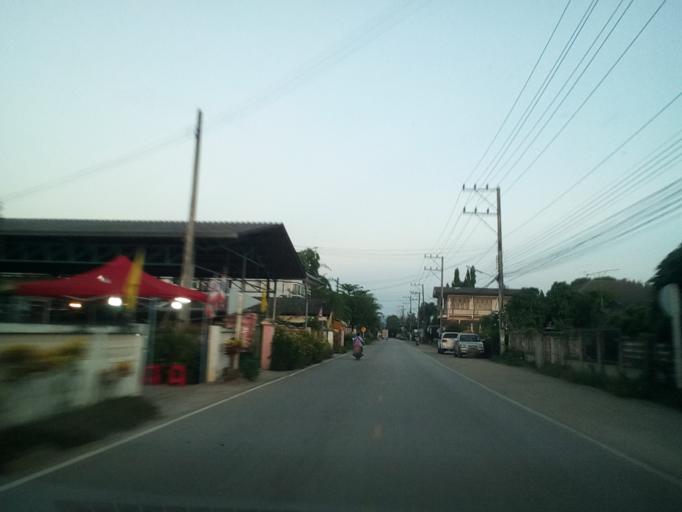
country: TH
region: Lamphun
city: Lamphun
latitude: 18.6360
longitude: 99.0426
